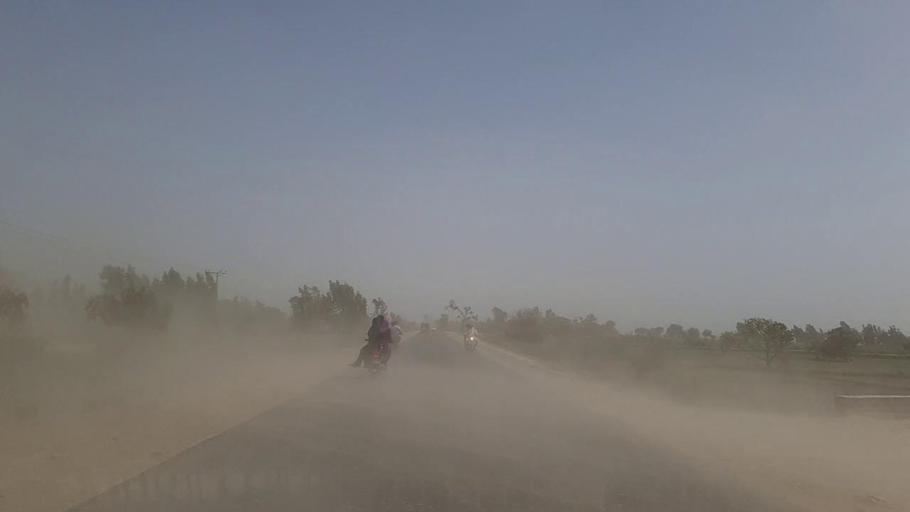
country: PK
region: Sindh
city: Tando Bago
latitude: 24.7945
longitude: 68.9519
